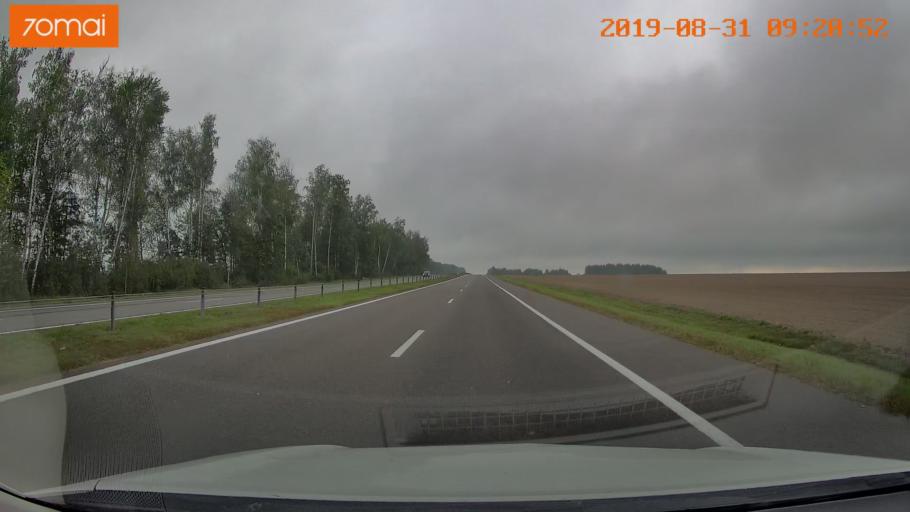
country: BY
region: Minsk
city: Byerazino
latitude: 53.7977
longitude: 28.8431
